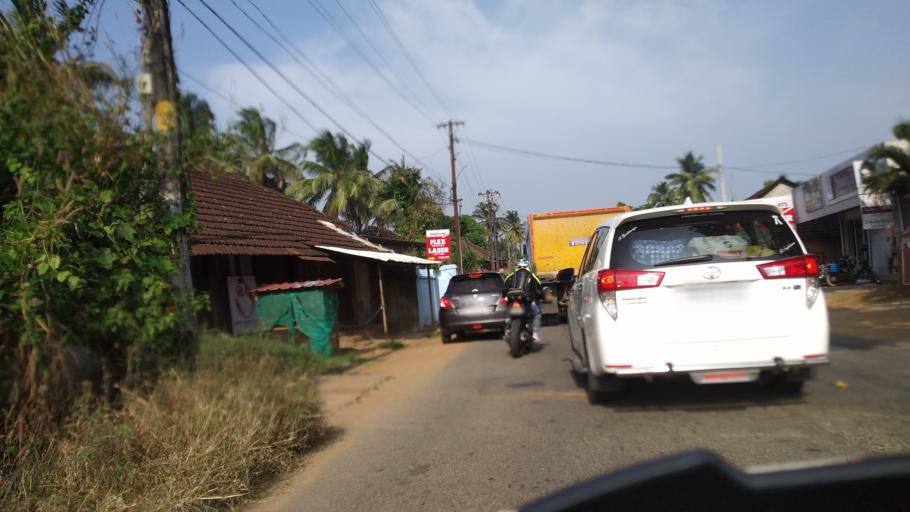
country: IN
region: Kerala
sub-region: Thrissur District
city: Chelakara
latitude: 10.5913
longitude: 76.5182
